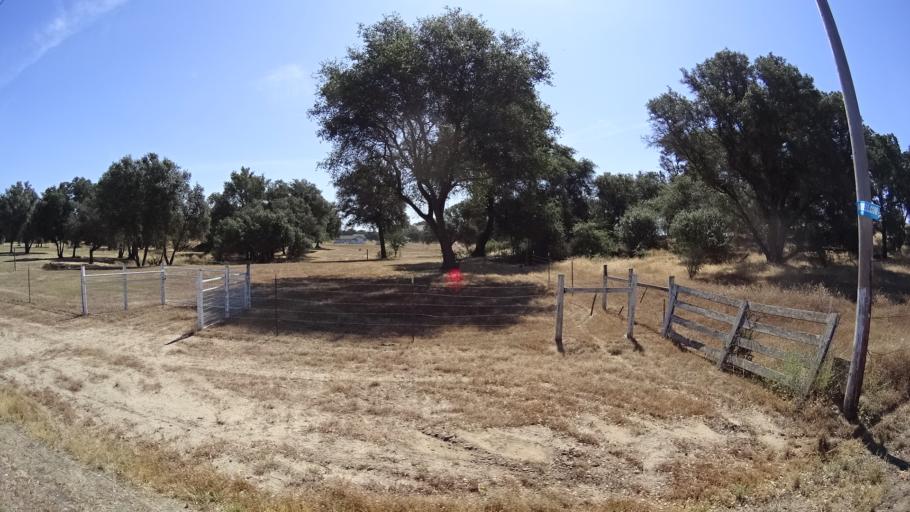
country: US
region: California
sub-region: Calaveras County
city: Rancho Calaveras
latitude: 38.1302
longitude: -120.9265
